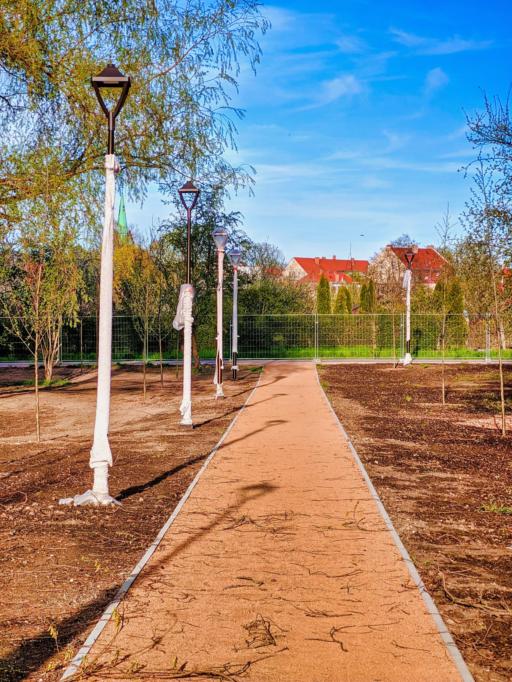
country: PL
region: Lubusz
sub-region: Powiat swiebodzinski
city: Swiebodzin
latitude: 52.2493
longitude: 15.5243
